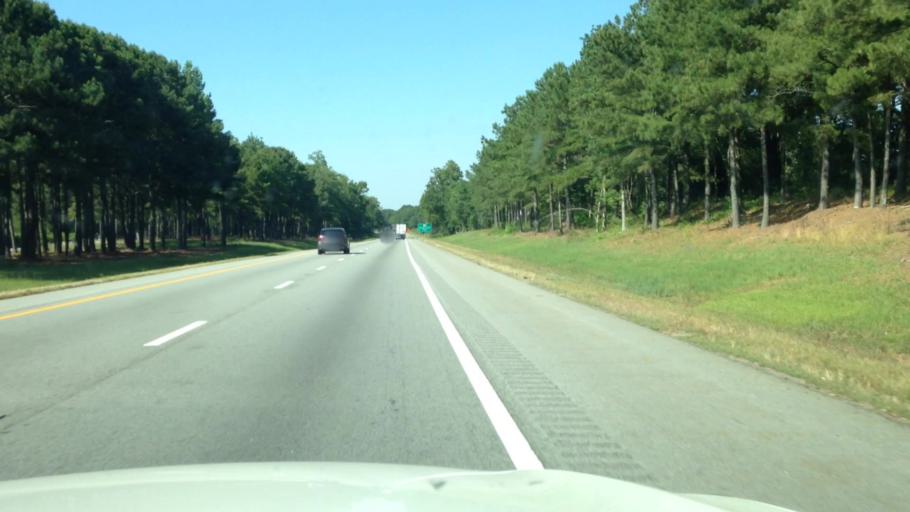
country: US
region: North Carolina
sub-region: Halifax County
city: Weldon
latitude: 36.4099
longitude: -77.6391
